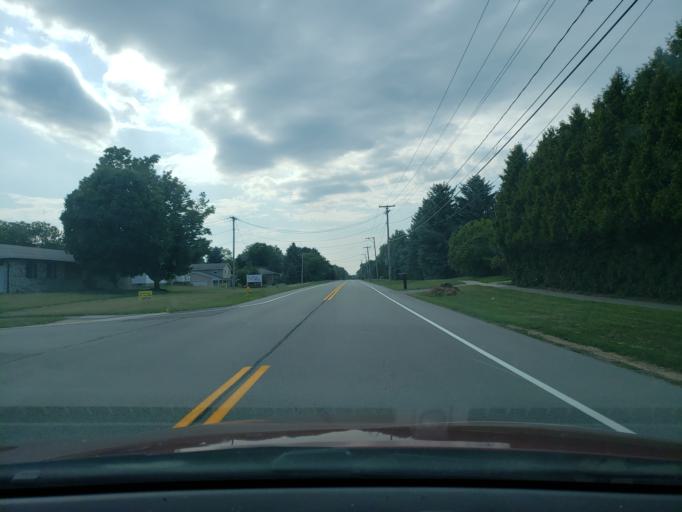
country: US
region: New York
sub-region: Monroe County
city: Greece
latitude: 43.2787
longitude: -77.7030
